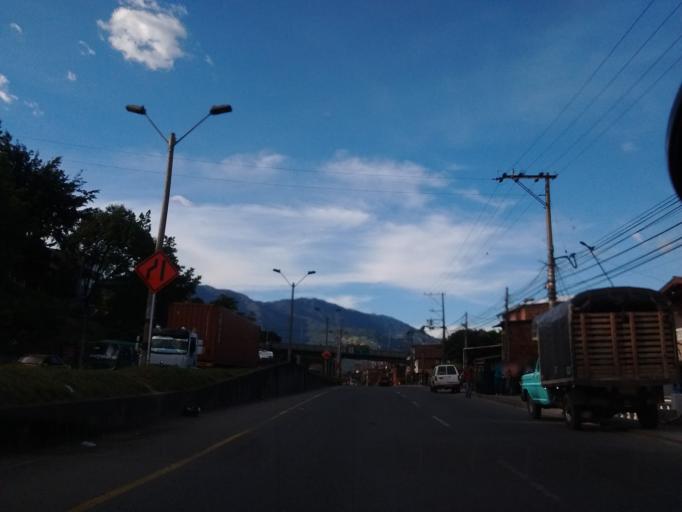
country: CO
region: Antioquia
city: Bello
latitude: 6.2999
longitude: -75.5591
